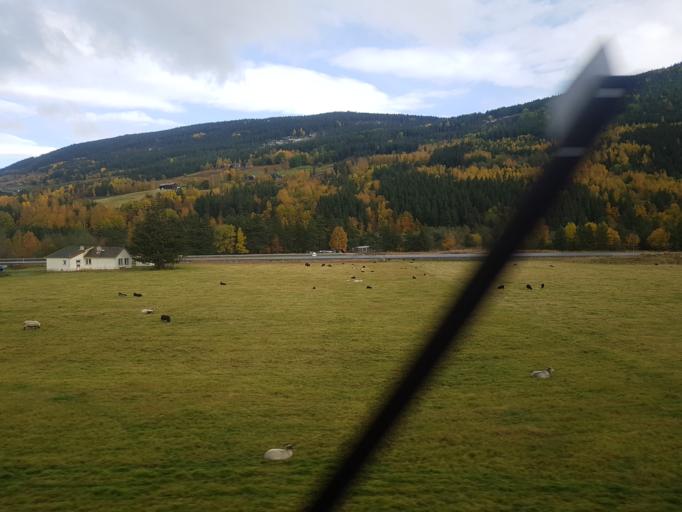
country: NO
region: Oppland
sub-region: Dovre
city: Dovre
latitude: 61.9865
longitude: 9.2407
